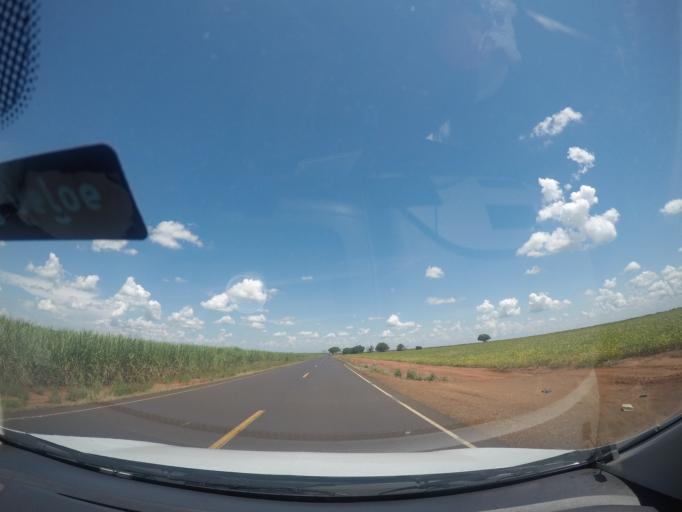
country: BR
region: Minas Gerais
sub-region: Frutal
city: Frutal
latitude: -19.7137
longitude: -48.7692
